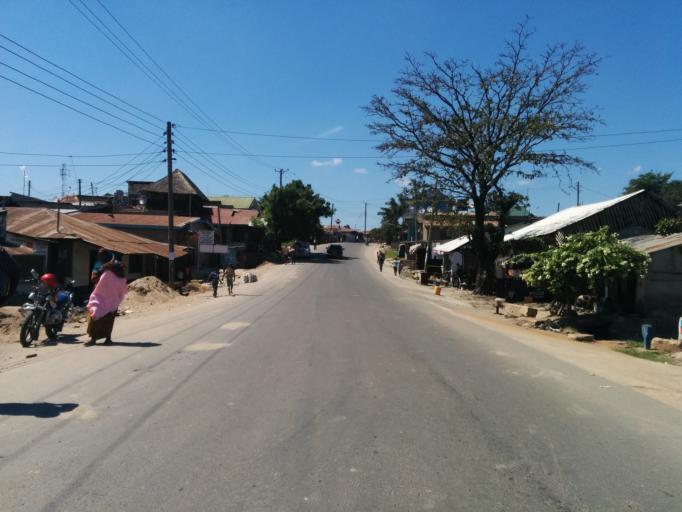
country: TZ
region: Dar es Salaam
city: Magomeni
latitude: -6.7963
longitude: 39.2412
